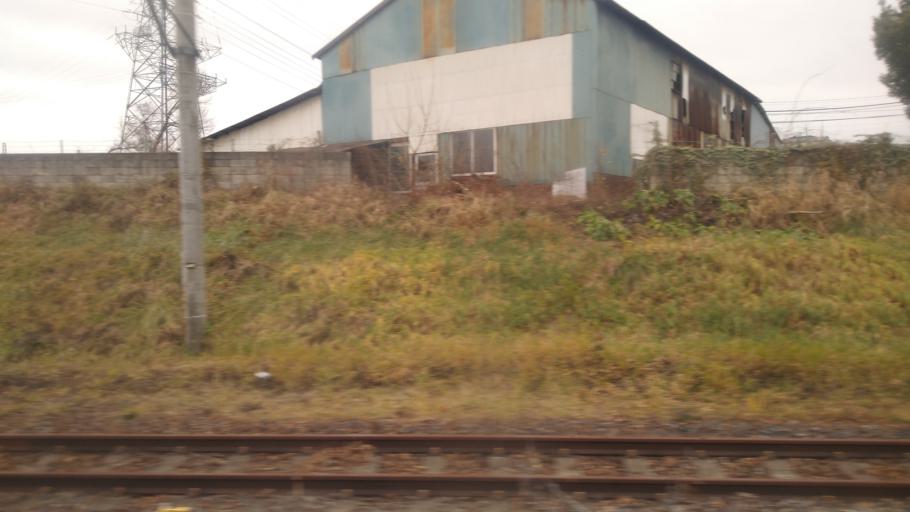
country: JP
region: Nagano
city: Shiojiri
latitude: 36.1107
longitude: 137.9449
